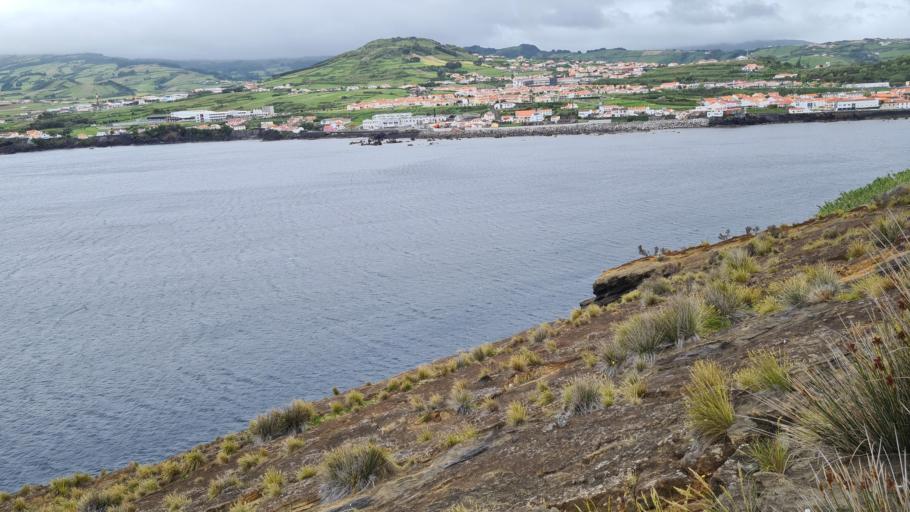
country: PT
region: Azores
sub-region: Horta
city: Horta
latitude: 38.5184
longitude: -28.6322
